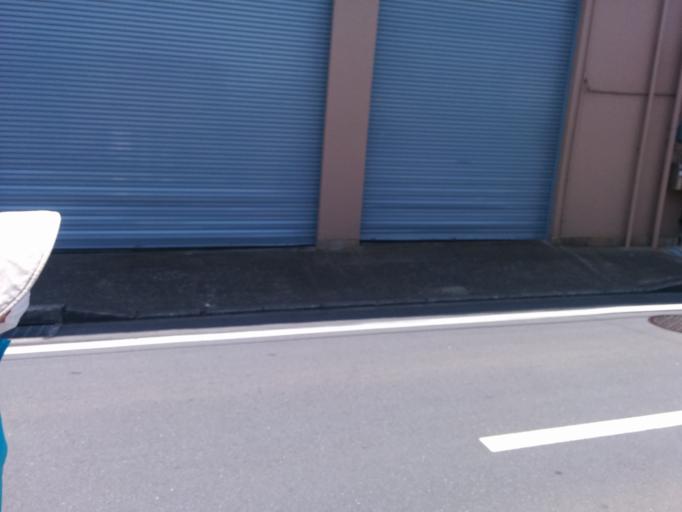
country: JP
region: Tokyo
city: Higashimurayama-shi
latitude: 35.7687
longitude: 139.4712
